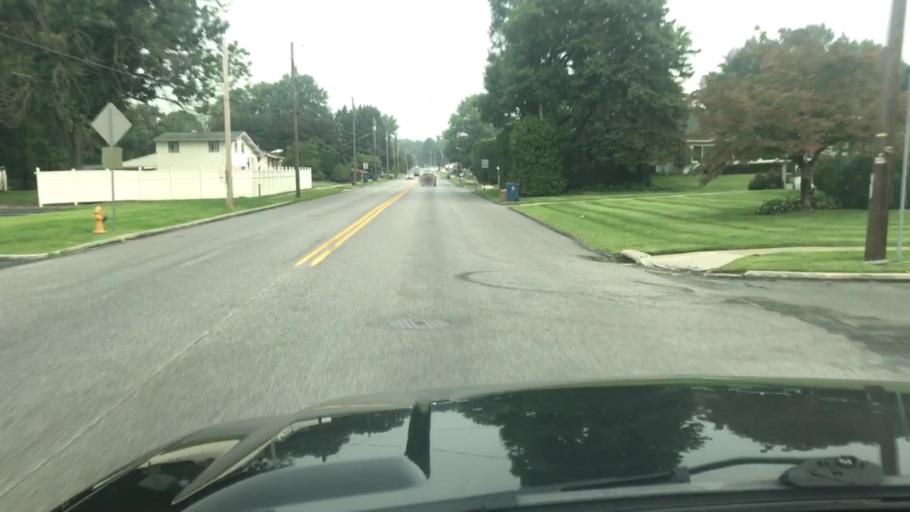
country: US
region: Pennsylvania
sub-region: Cumberland County
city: Shiremanstown
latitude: 40.2339
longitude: -76.9570
